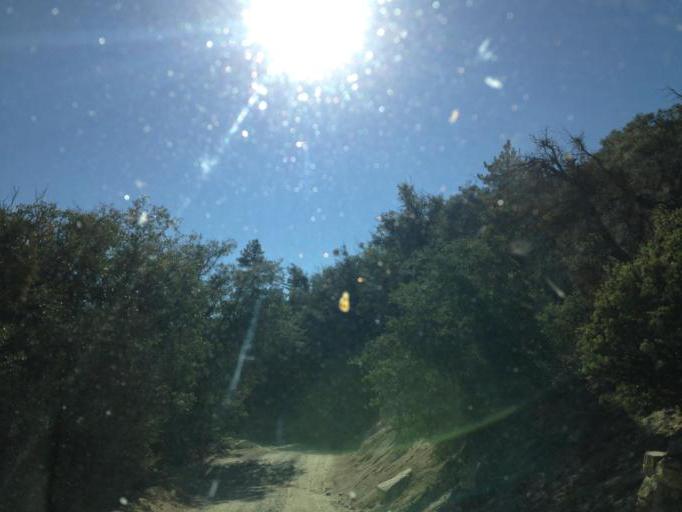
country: US
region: California
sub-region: Riverside County
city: Idyllwild-Pine Cove
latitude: 33.8134
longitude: -116.7475
